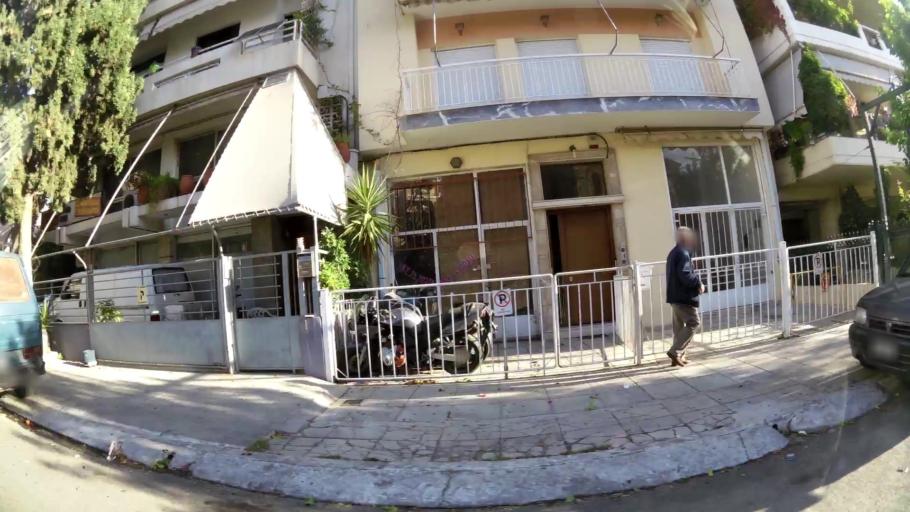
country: GR
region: Attica
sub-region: Nomos Piraios
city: Agios Ioannis Rentis
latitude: 37.9762
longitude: 23.6621
